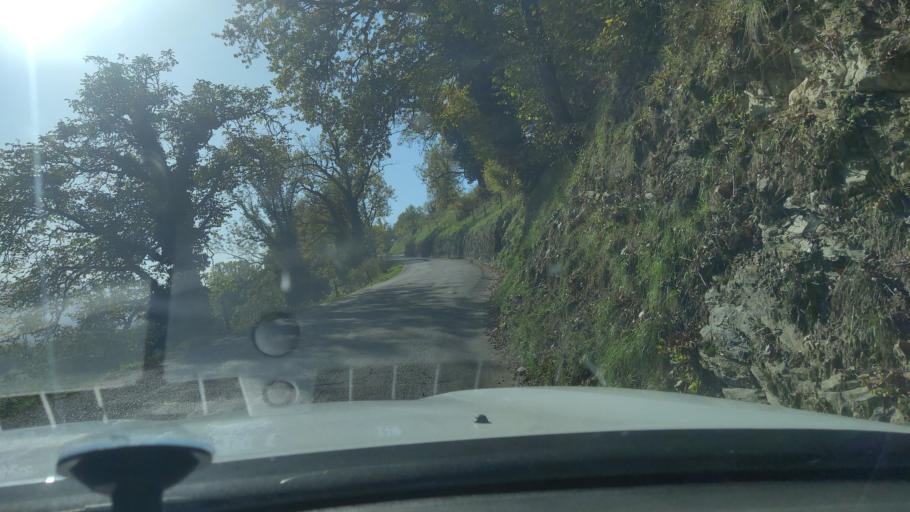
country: FR
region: Rhone-Alpes
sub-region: Departement de la Savoie
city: Frontenex
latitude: 45.6442
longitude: 6.3248
